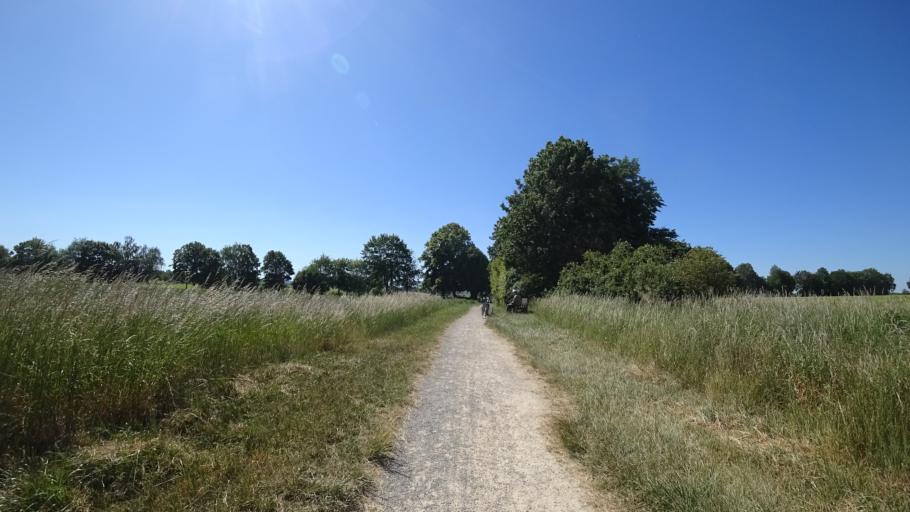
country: DE
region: North Rhine-Westphalia
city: Erwitte
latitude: 51.6230
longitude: 8.3653
